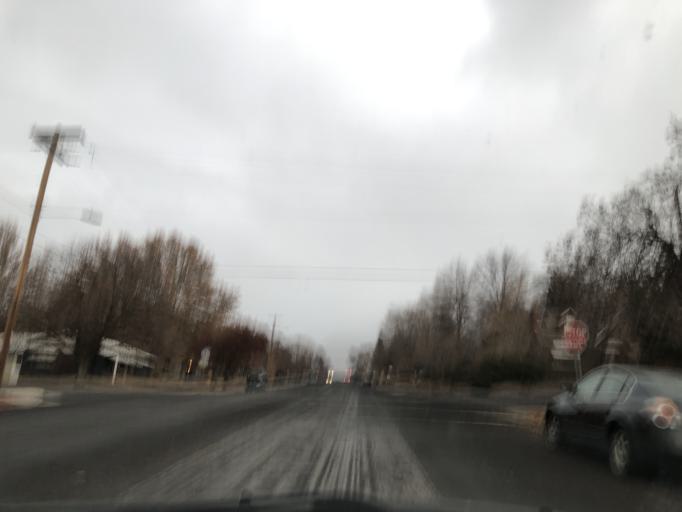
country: US
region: Utah
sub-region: Cache County
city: Logan
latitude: 41.7370
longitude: -111.8276
